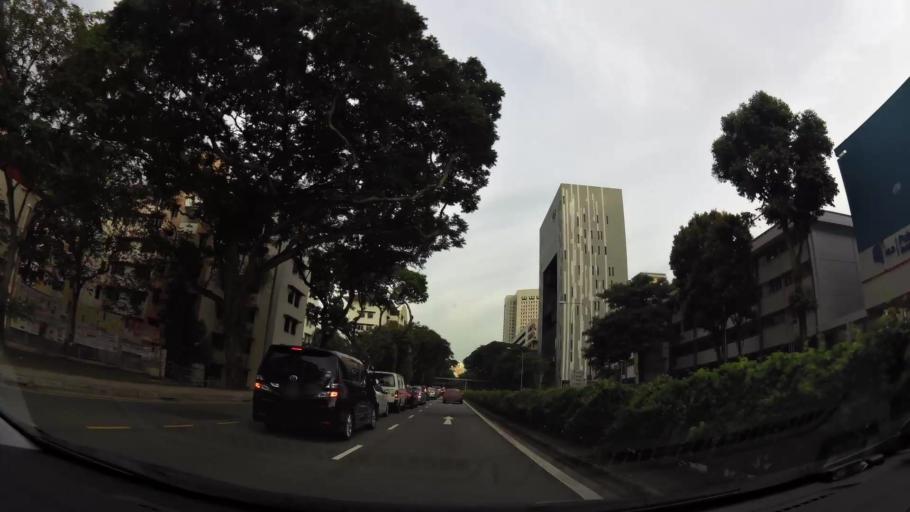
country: SG
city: Singapore
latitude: 1.2846
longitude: 103.8158
